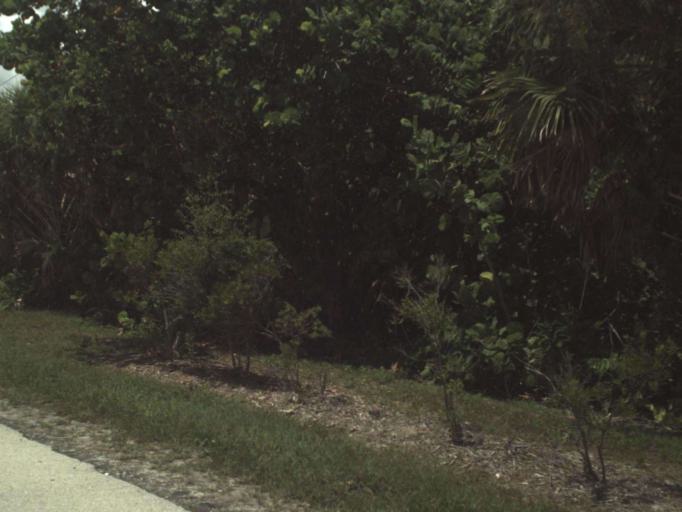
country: US
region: Florida
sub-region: Martin County
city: Jensen Beach
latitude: 27.2466
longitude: -80.1930
